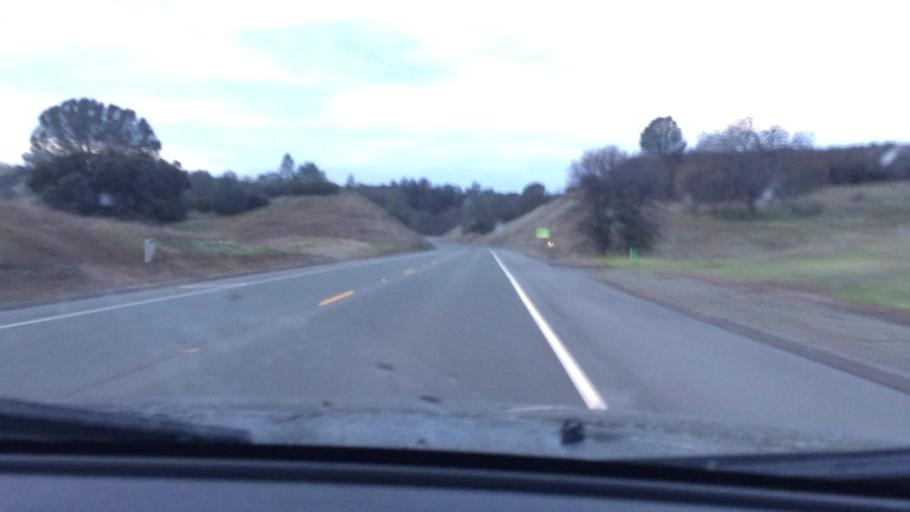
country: US
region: California
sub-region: Amador County
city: Ione
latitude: 38.4097
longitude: -120.8881
